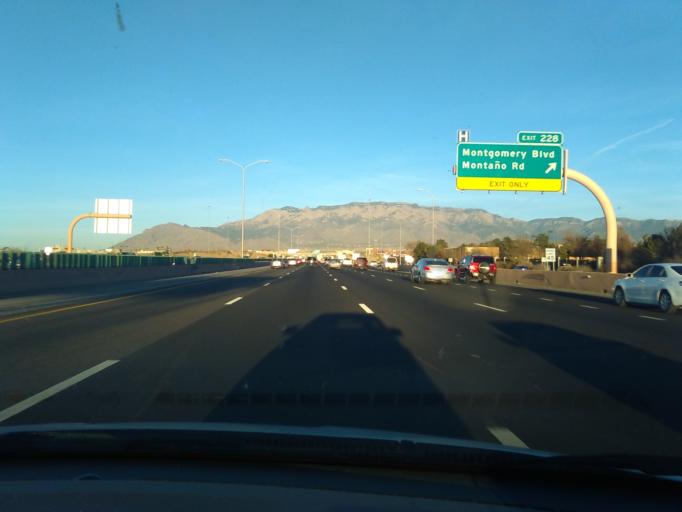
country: US
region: New Mexico
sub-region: Bernalillo County
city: Lee Acres
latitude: 35.1296
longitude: -106.6146
